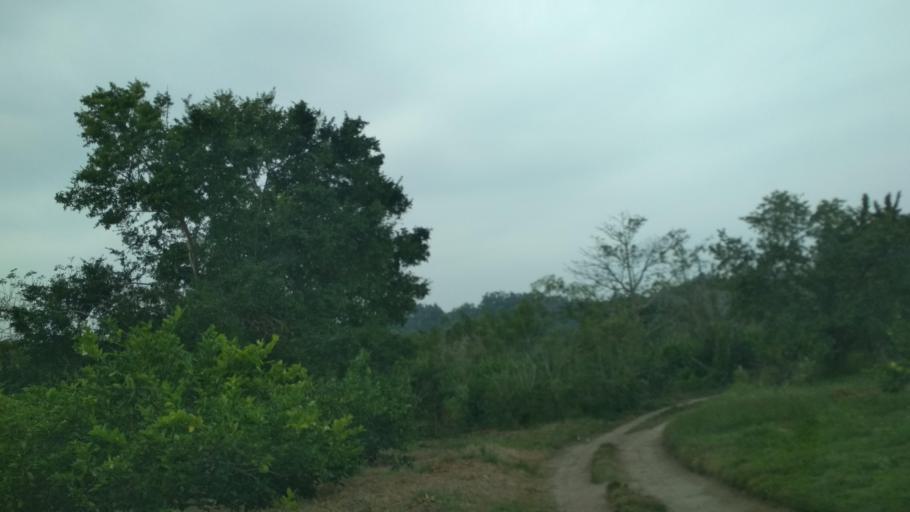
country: MM
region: Kayah
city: Loikaw
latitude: 20.2142
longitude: 97.3309
